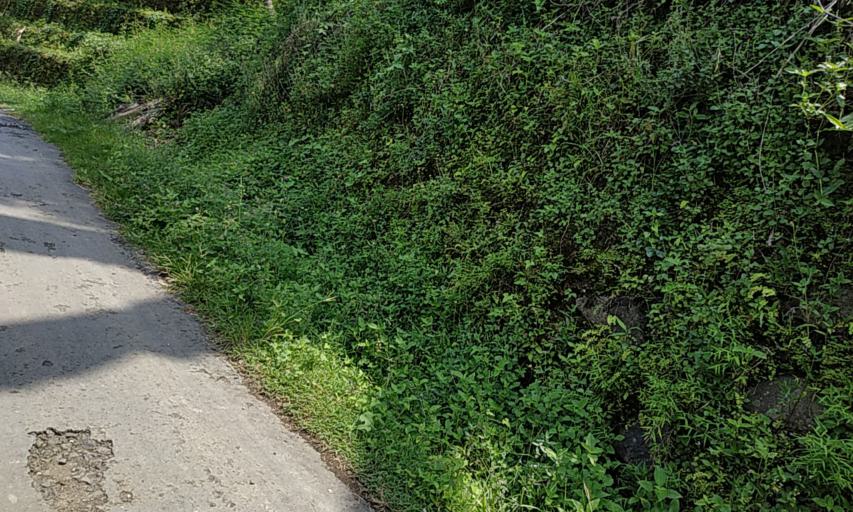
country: ID
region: Central Java
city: Kutoarjo
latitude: -7.6230
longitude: 109.7257
